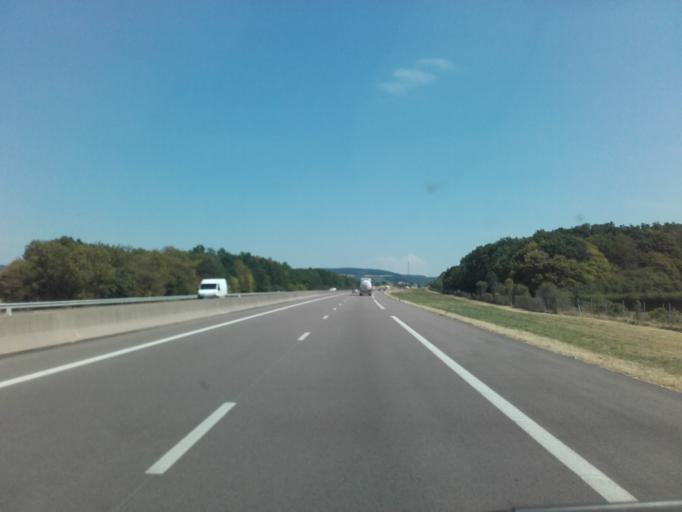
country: FR
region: Bourgogne
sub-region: Departement de la Cote-d'Or
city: Vitteaux
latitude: 47.3530
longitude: 4.4450
